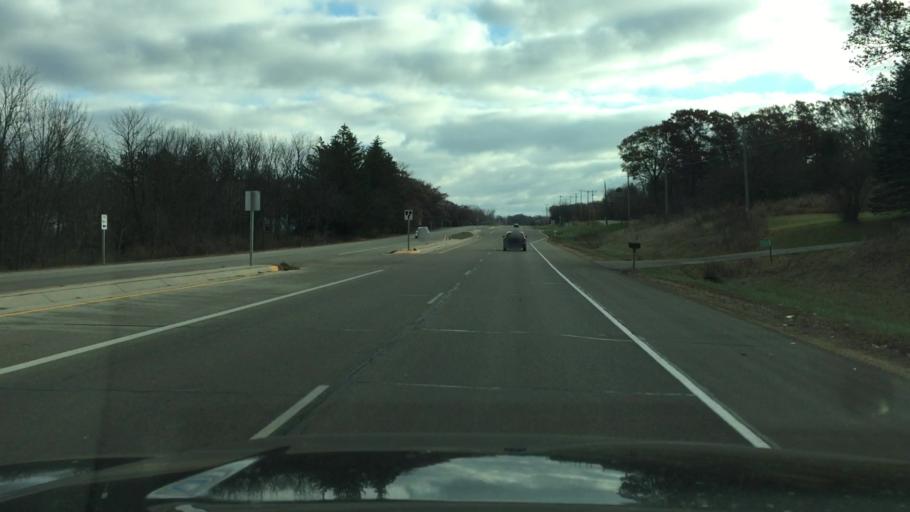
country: US
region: Wisconsin
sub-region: Walworth County
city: Williams Bay
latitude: 42.5829
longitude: -88.5149
